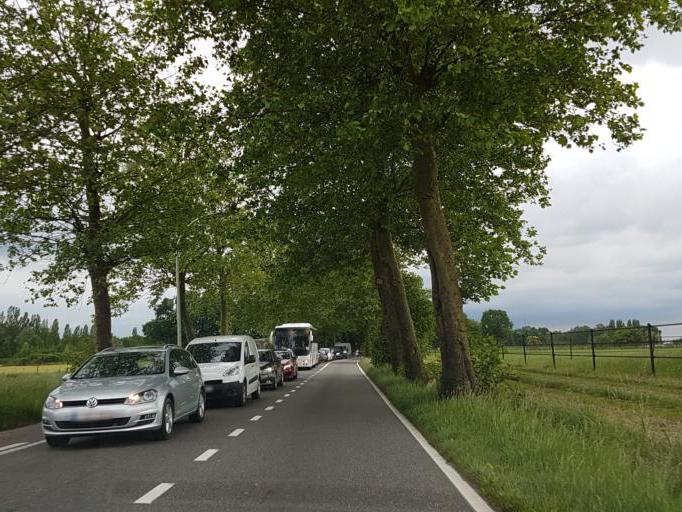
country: BE
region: Flanders
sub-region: Provincie Antwerpen
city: Nijlen
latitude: 51.1785
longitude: 4.6306
